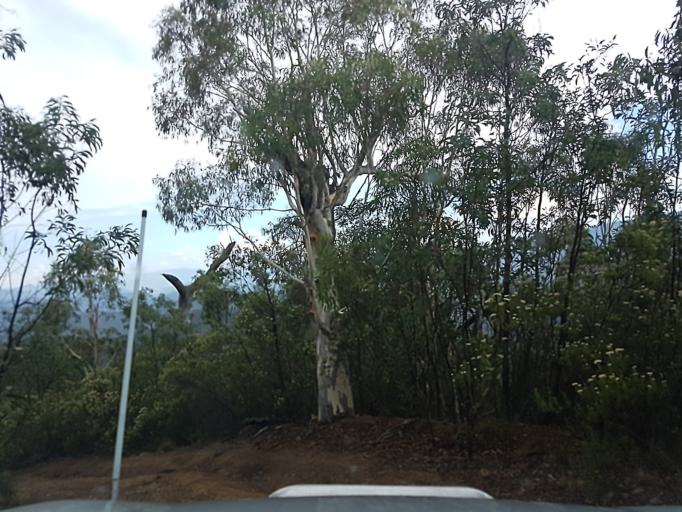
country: AU
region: New South Wales
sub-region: Snowy River
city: Jindabyne
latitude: -36.9120
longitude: 148.3346
